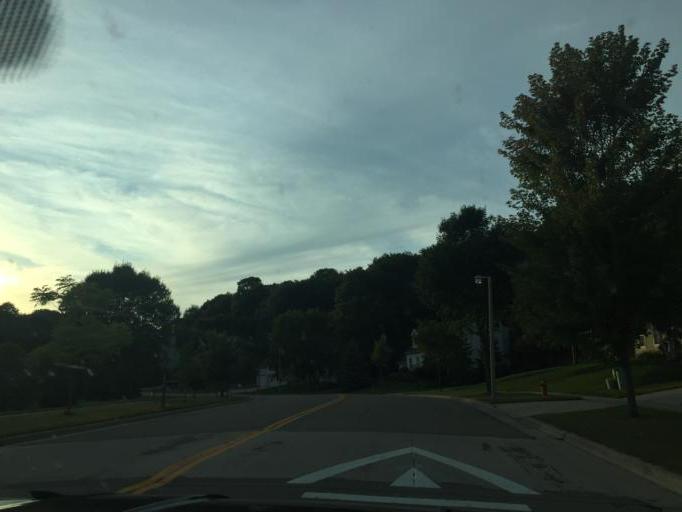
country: US
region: Minnesota
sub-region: Olmsted County
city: Rochester
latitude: 44.0098
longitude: -92.4935
